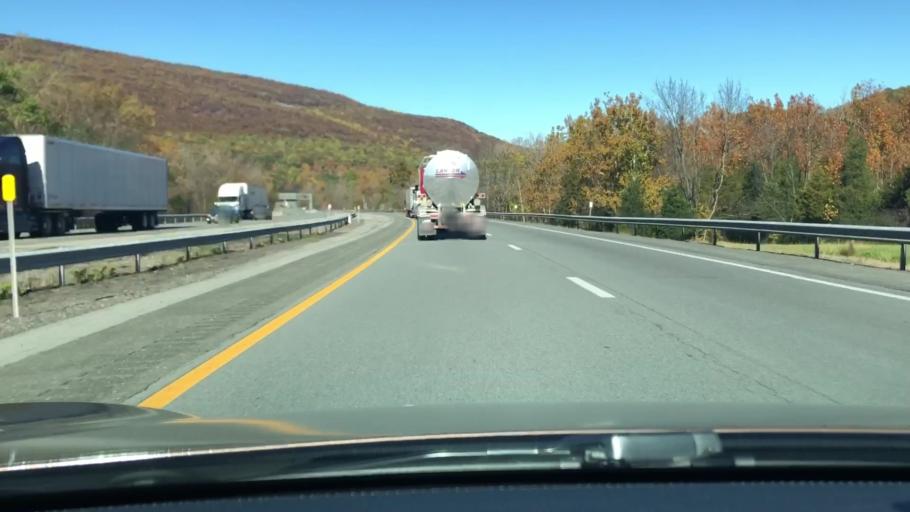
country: US
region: New York
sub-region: Orange County
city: Woodbury
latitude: 41.3697
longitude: -74.1015
